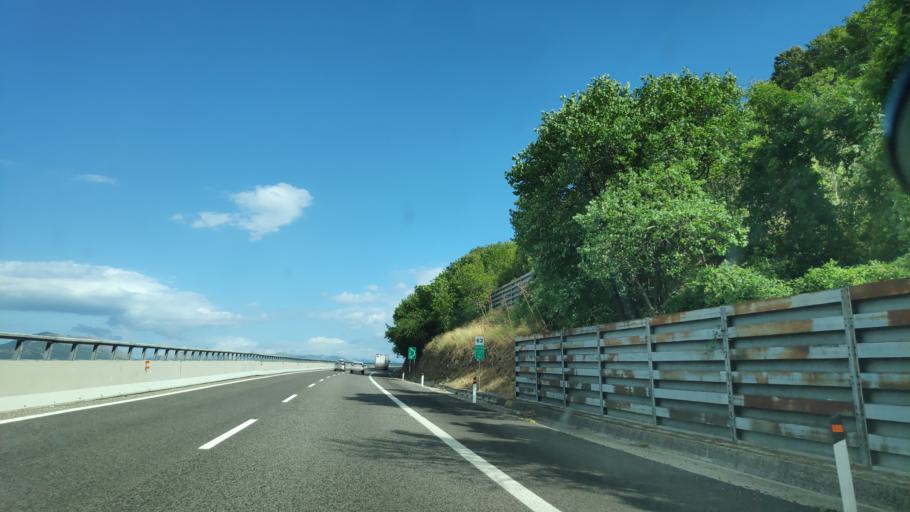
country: IT
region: Campania
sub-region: Provincia di Salerno
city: Sicignano degli Alburni
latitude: 40.5908
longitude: 15.3298
